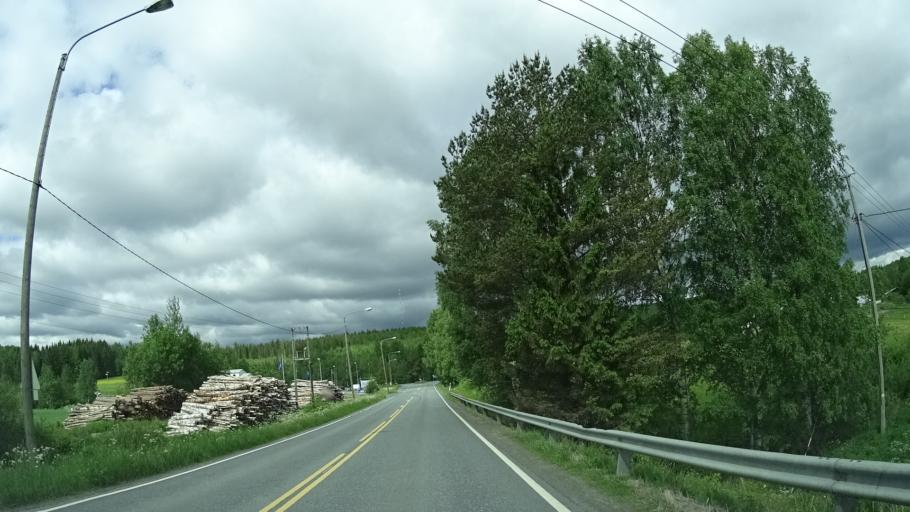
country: FI
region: Central Finland
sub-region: Jyvaeskylae
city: Korpilahti
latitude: 62.0316
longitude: 25.6055
